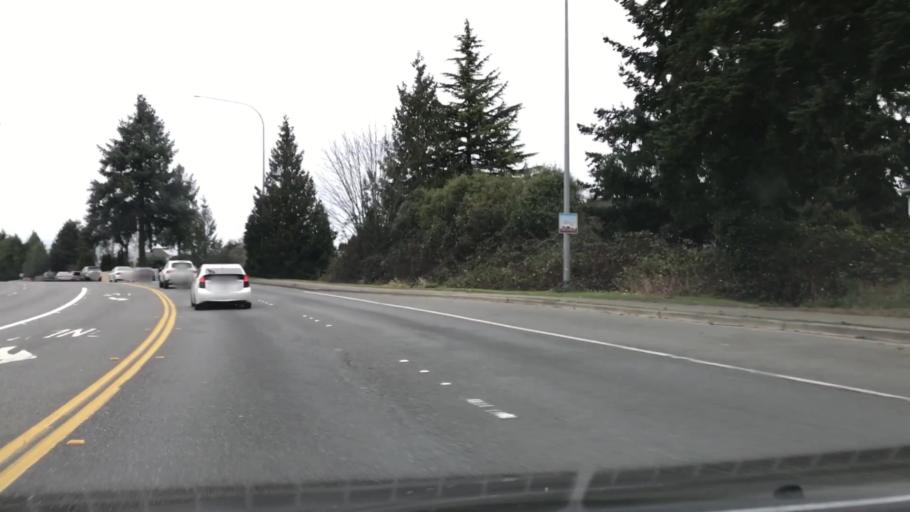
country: US
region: Washington
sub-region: King County
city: East Hill-Meridian
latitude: 47.4031
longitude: -122.1972
